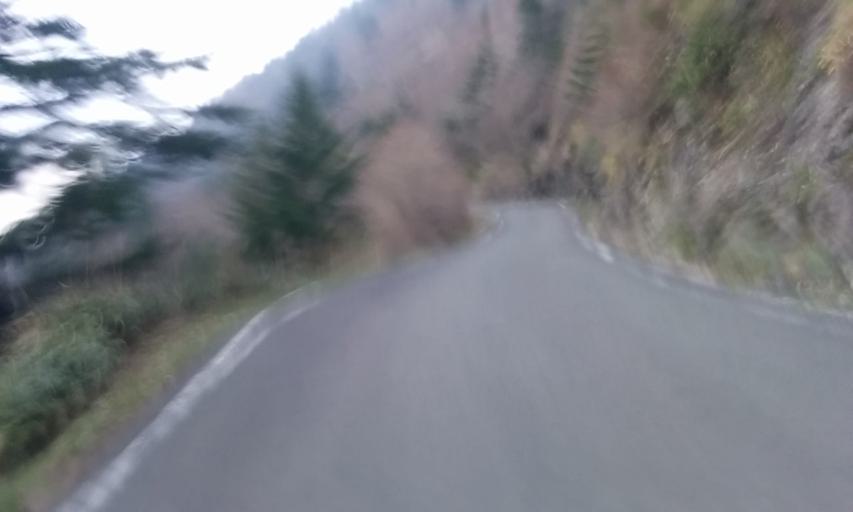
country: JP
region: Ehime
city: Saijo
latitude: 33.7848
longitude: 133.2421
